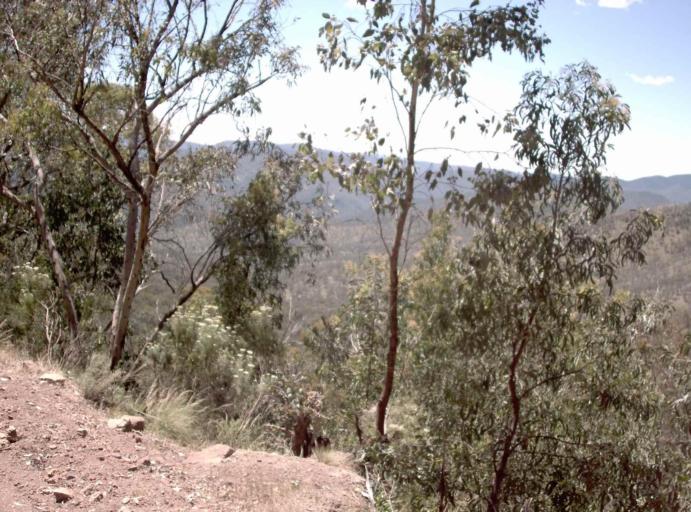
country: AU
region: New South Wales
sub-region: Snowy River
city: Jindabyne
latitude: -36.9859
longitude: 148.3005
